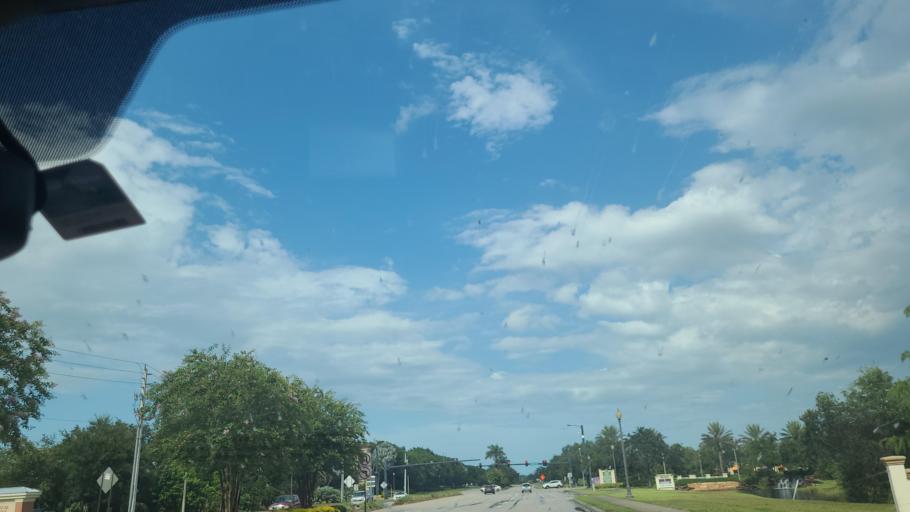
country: US
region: Florida
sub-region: Martin County
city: North River Shores
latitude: 27.2100
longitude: -80.3302
